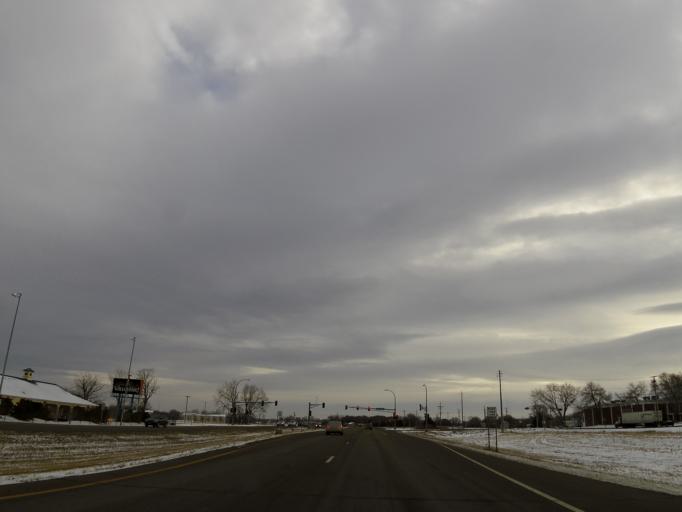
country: US
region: Minnesota
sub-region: Hennepin County
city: Eden Prairie
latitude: 44.7964
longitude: -93.4522
